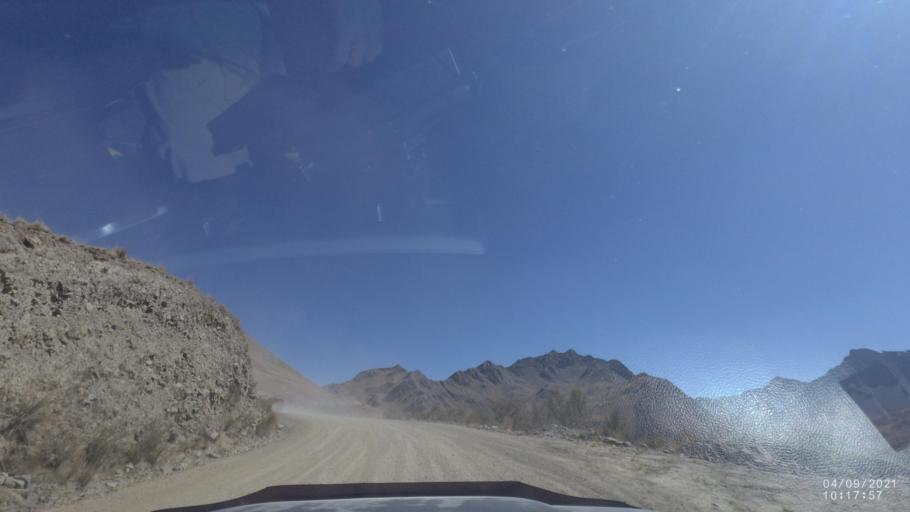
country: BO
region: Cochabamba
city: Sipe Sipe
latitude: -17.3218
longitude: -66.4213
